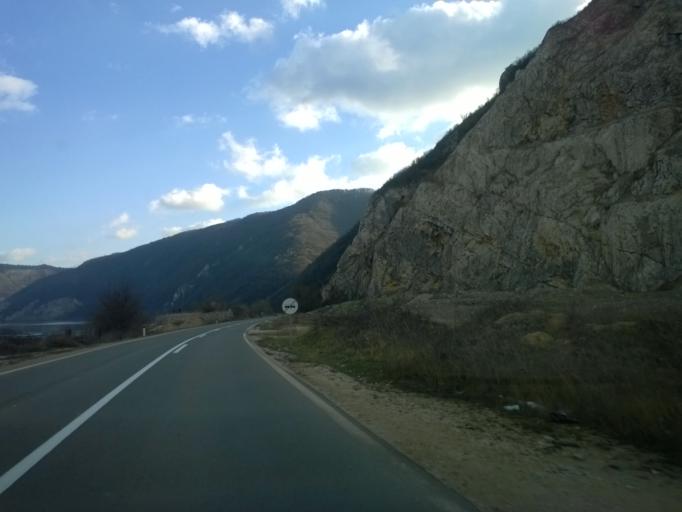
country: RO
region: Caras-Severin
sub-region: Comuna Pescari
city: Coronini
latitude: 44.6601
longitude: 21.7006
